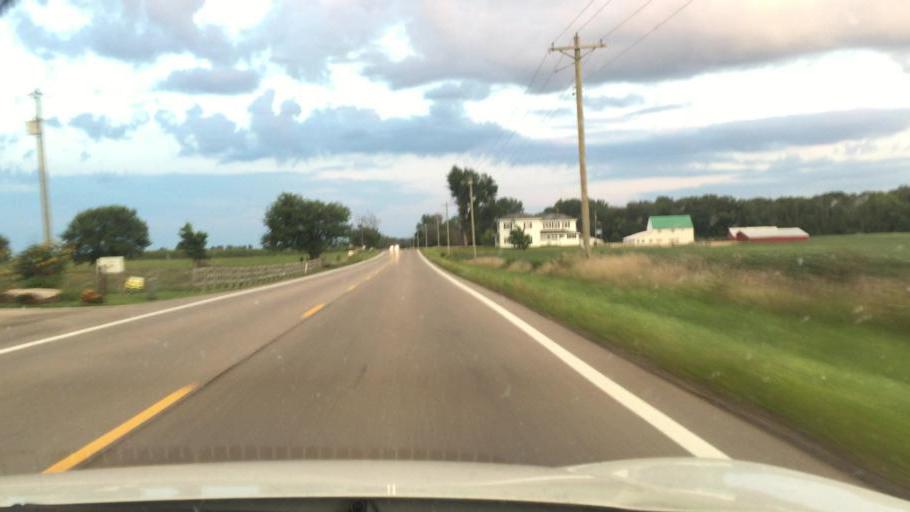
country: US
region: Ohio
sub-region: Champaign County
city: Mechanicsburg
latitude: 40.0537
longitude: -83.5284
